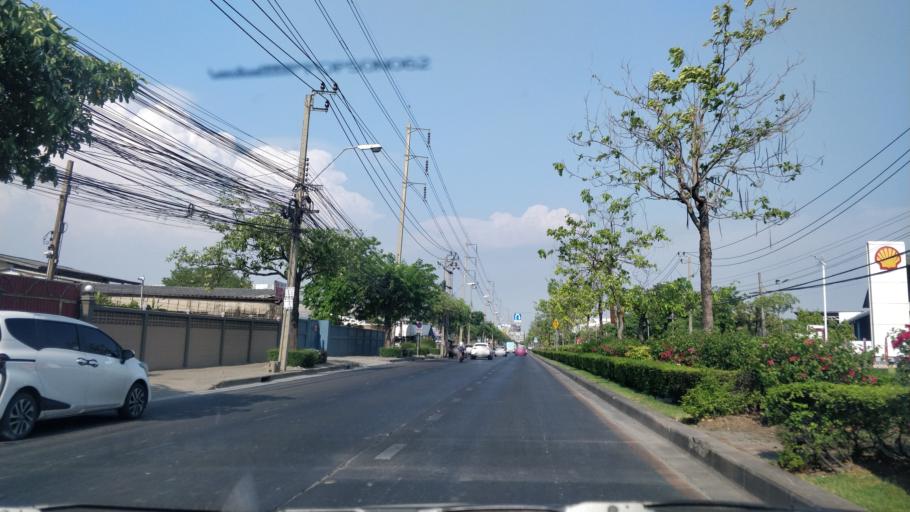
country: TH
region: Bangkok
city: Suan Luang
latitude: 13.7192
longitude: 100.6716
